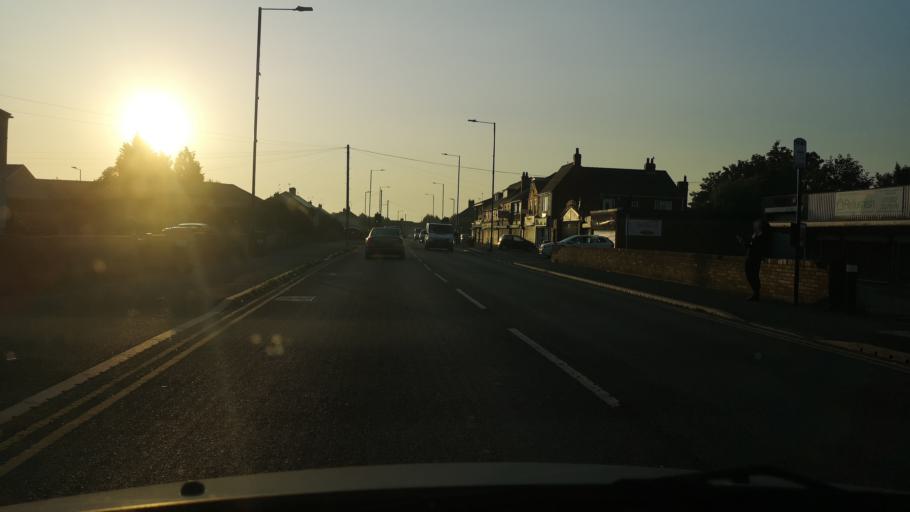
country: GB
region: England
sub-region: Doncaster
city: Stainforth
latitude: 53.5848
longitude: -1.0215
